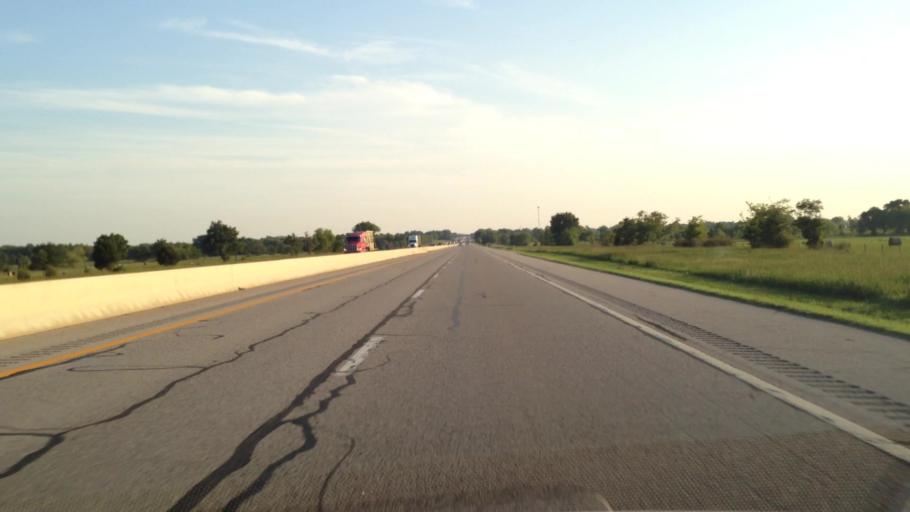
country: US
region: Oklahoma
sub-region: Ottawa County
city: Fairland
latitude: 36.7933
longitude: -94.8840
